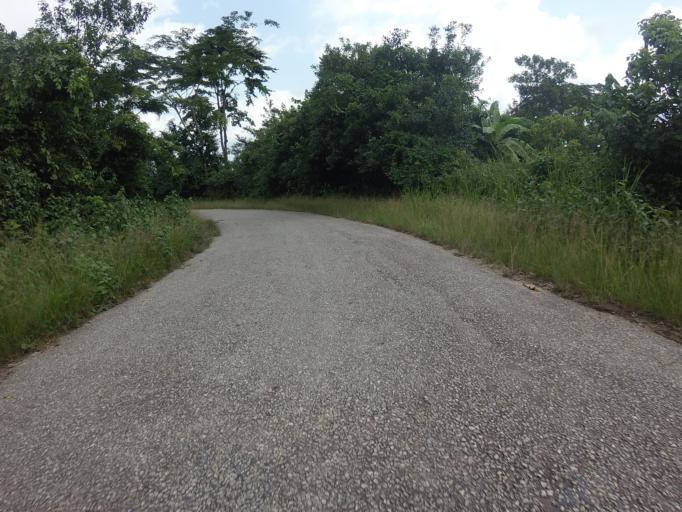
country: GH
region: Volta
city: Kpandu
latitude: 6.8352
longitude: 0.4261
